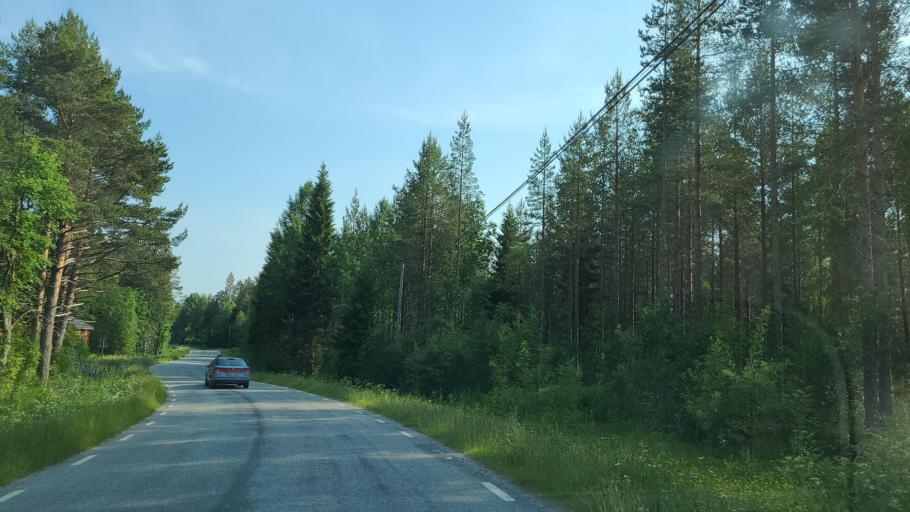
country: SE
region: Vaesterbotten
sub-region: Skelleftea Kommun
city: Burea
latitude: 64.3522
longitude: 21.3352
